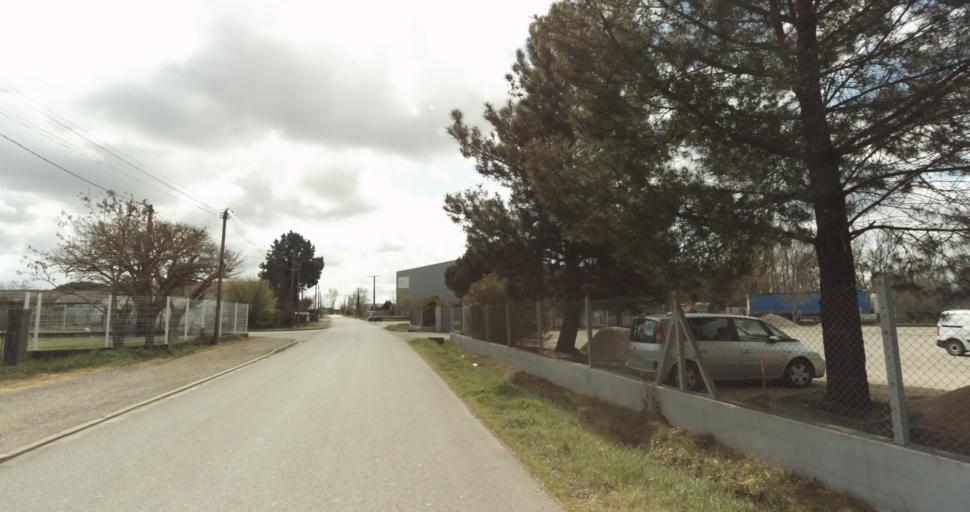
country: FR
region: Midi-Pyrenees
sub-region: Departement de la Haute-Garonne
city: Auterive
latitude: 43.3659
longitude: 1.4620
